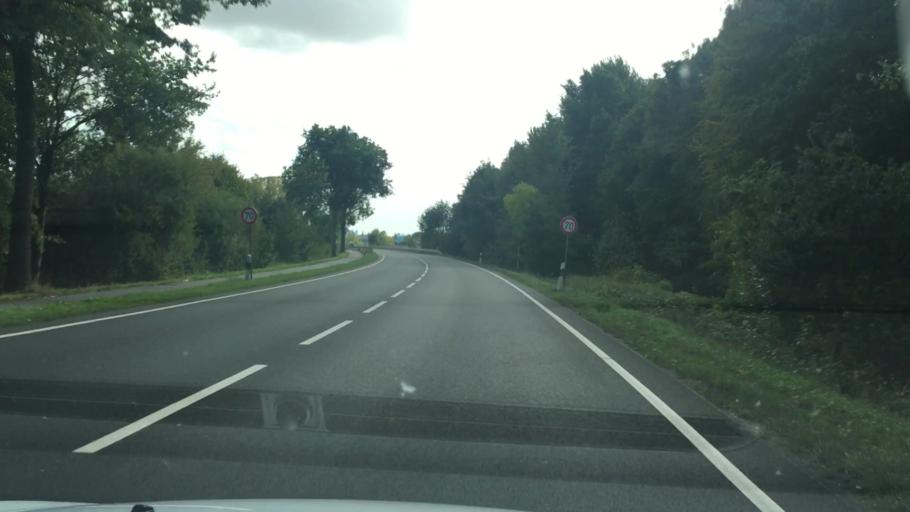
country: DE
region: Lower Saxony
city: Diepholz
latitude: 52.6231
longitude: 8.3636
